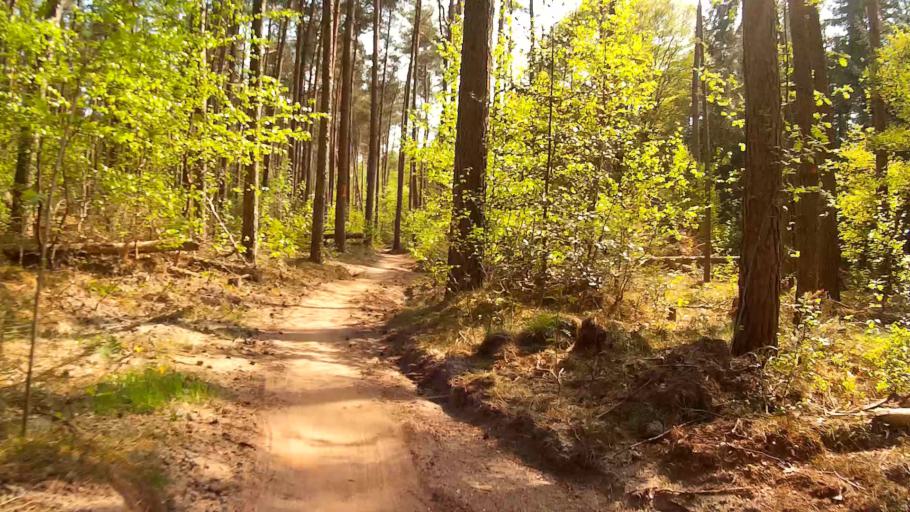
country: NL
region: Utrecht
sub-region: Gemeente Baarn
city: Baarn
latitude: 52.1876
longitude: 5.2381
